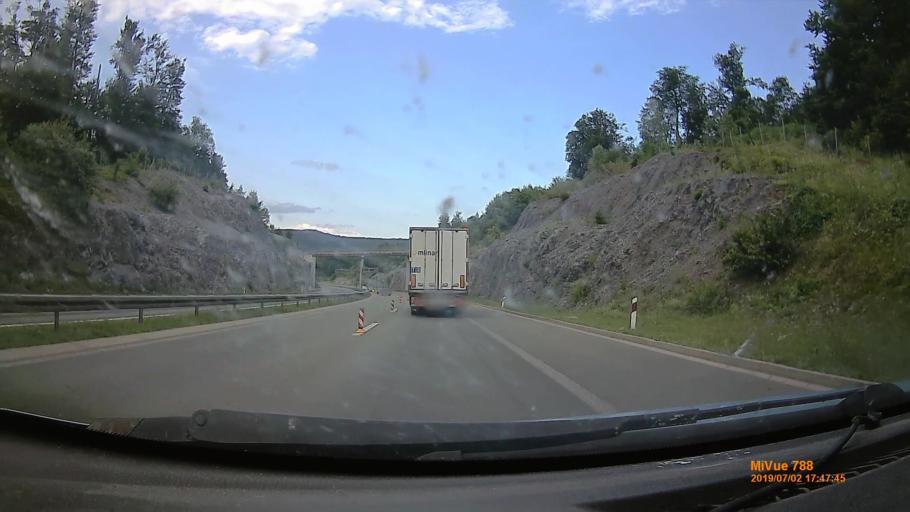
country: HR
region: Primorsko-Goranska
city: Vrbovsko
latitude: 45.3582
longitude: 15.0708
